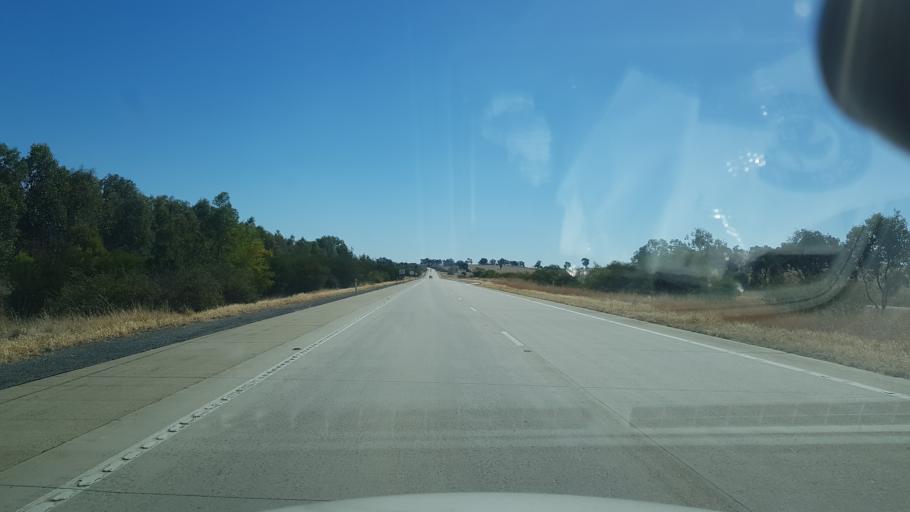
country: AU
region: New South Wales
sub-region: Greater Hume Shire
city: Jindera
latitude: -35.9264
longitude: 147.0711
